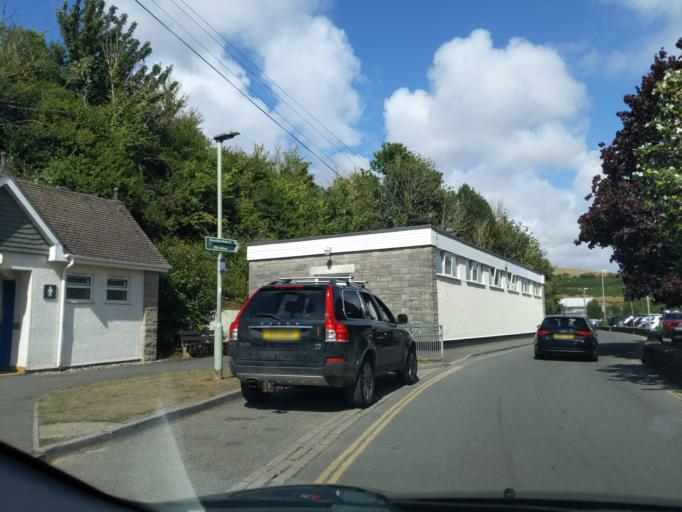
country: GB
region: England
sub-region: Devon
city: Salcombe
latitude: 50.2402
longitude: -3.7698
